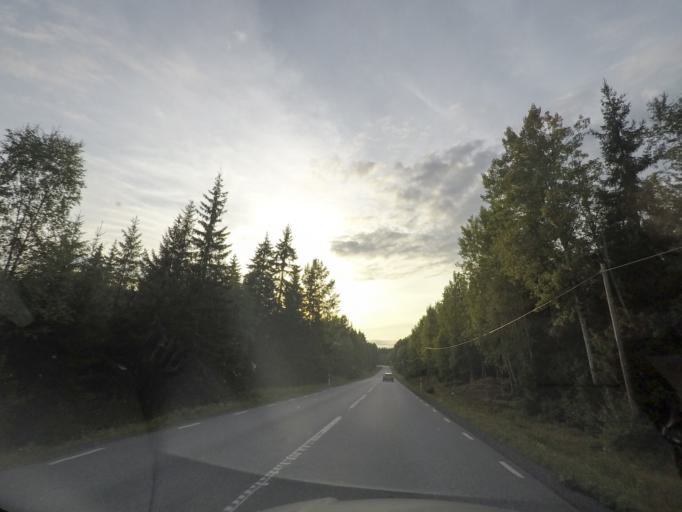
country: SE
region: OErebro
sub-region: Nora Kommun
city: As
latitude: 59.5198
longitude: 14.9064
